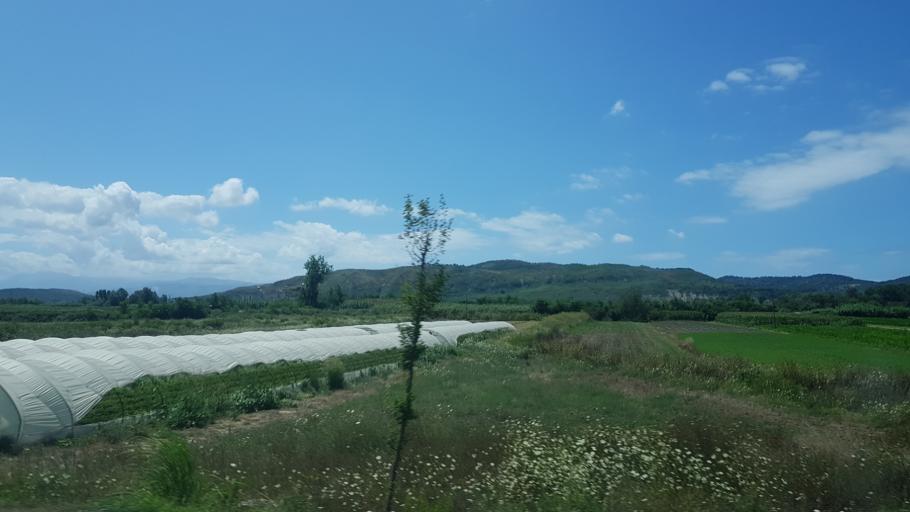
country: AL
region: Fier
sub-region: Rrethi i Fierit
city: Frakulla e Madhe
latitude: 40.6083
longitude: 19.5353
